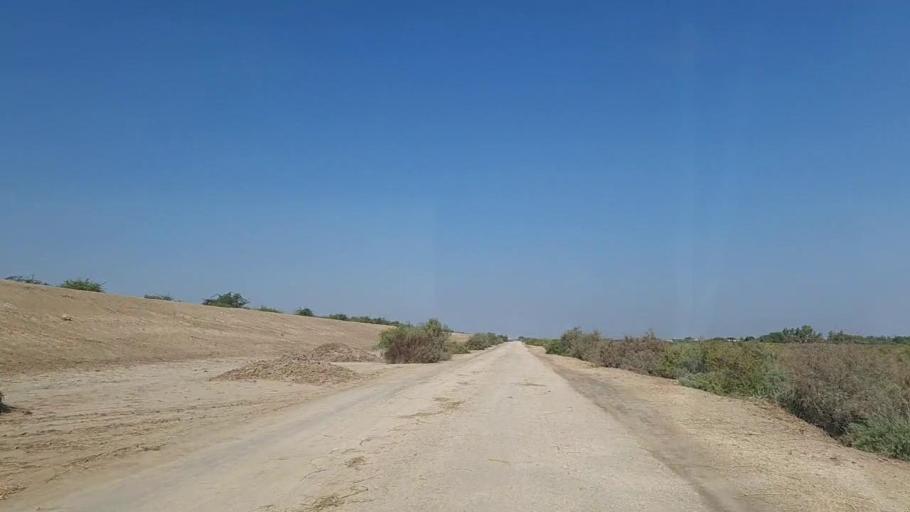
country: PK
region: Sindh
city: Chuhar Jamali
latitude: 24.4544
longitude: 67.9991
